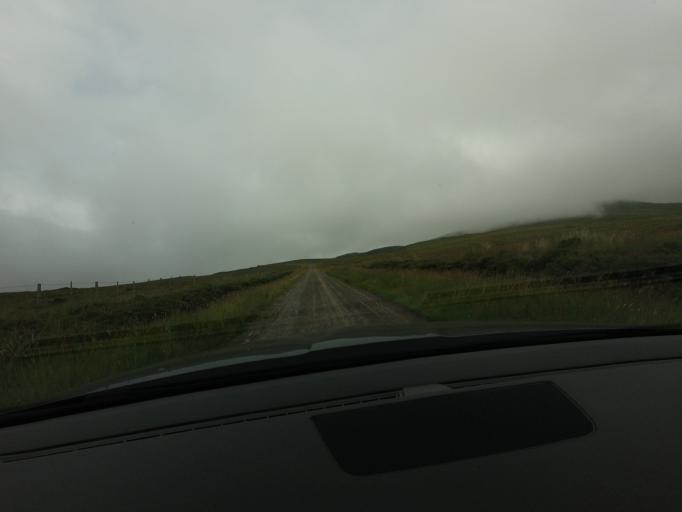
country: GB
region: Scotland
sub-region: Highland
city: Golspie
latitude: 58.4613
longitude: -4.3906
